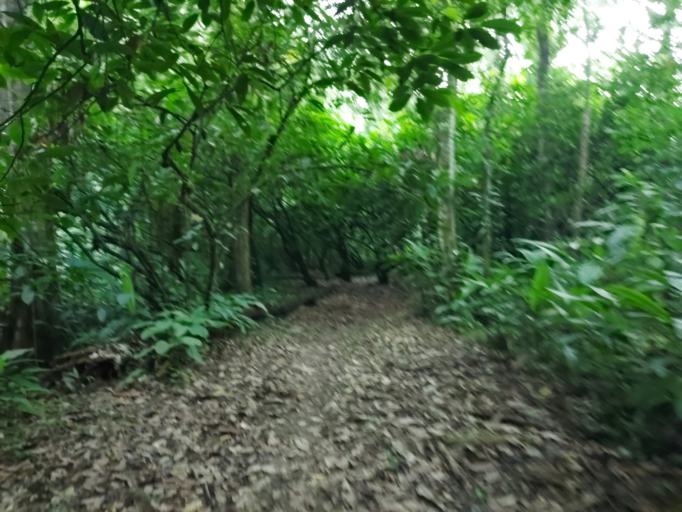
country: PA
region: Bocas del Toro
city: Barranco
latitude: 9.6458
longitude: -82.7875
